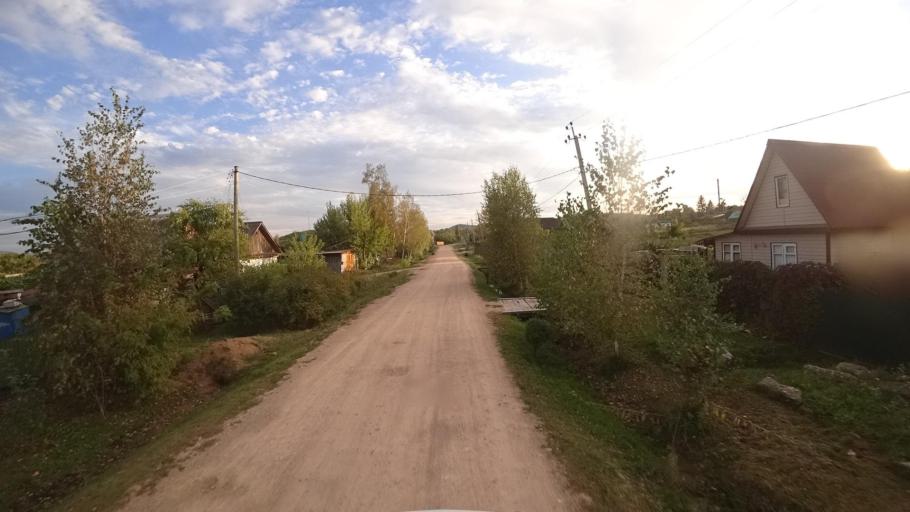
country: RU
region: Primorskiy
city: Yakovlevka
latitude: 44.4247
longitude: 133.4805
